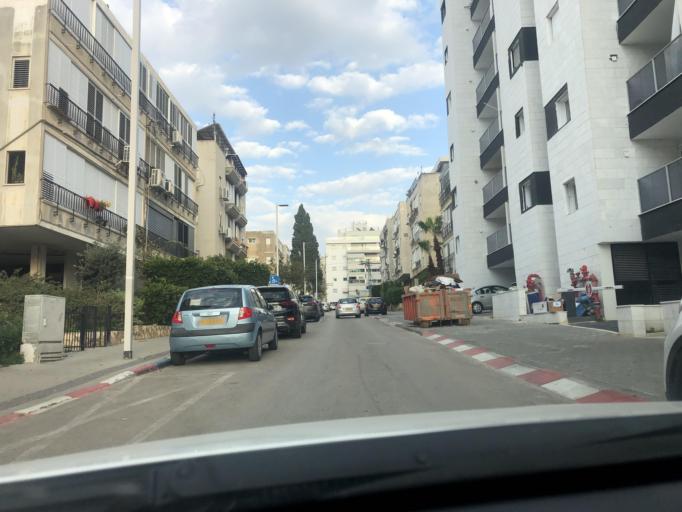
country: IL
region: Tel Aviv
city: Bat Yam
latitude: 32.0227
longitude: 34.7531
